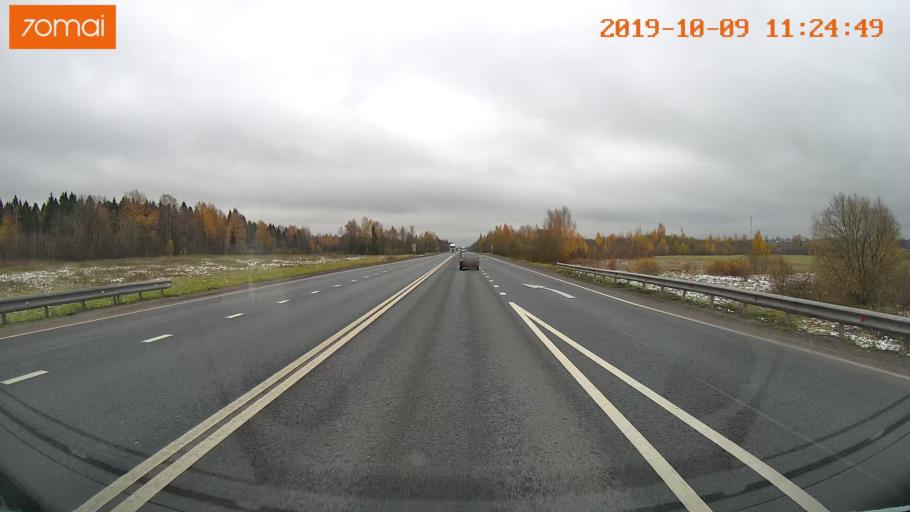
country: RU
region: Vologda
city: Vologda
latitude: 59.1077
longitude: 39.9841
